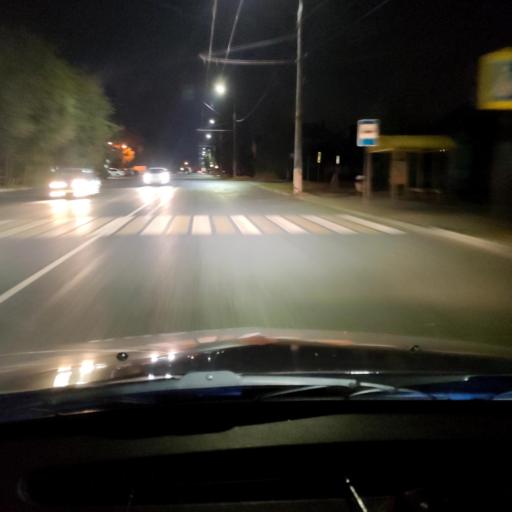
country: RU
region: Voronezj
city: Voronezh
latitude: 51.6984
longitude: 39.1886
